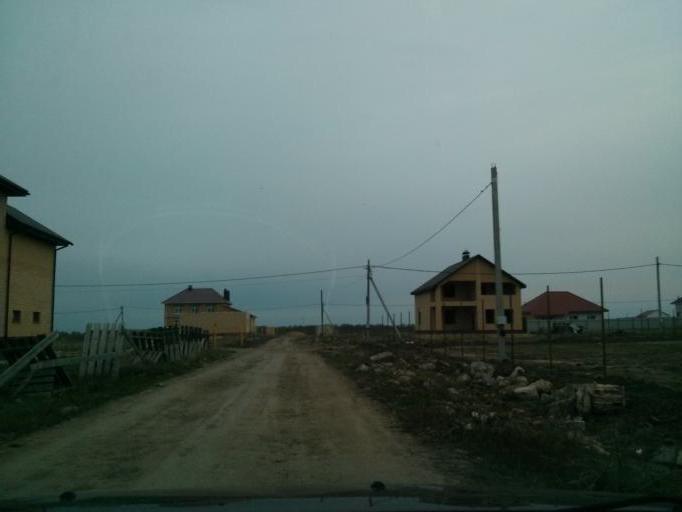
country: RU
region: Vladimir
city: Murom
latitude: 55.5447
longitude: 42.0654
